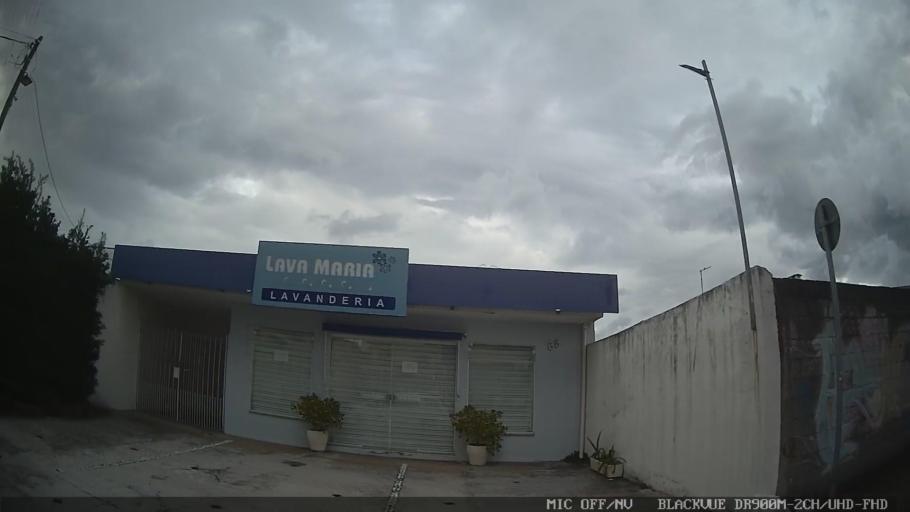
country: BR
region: Sao Paulo
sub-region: Mogi das Cruzes
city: Mogi das Cruzes
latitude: -23.5330
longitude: -46.1977
